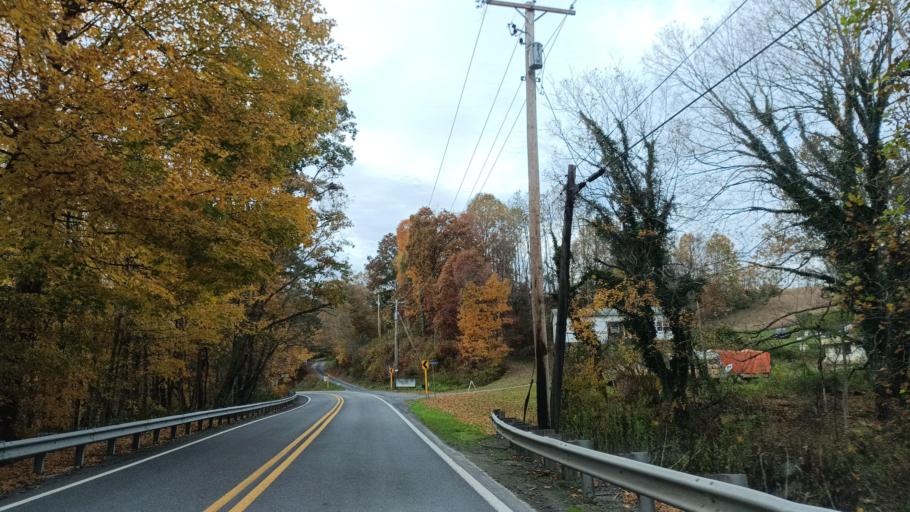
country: US
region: West Virginia
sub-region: Taylor County
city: Grafton
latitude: 39.3347
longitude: -79.8729
